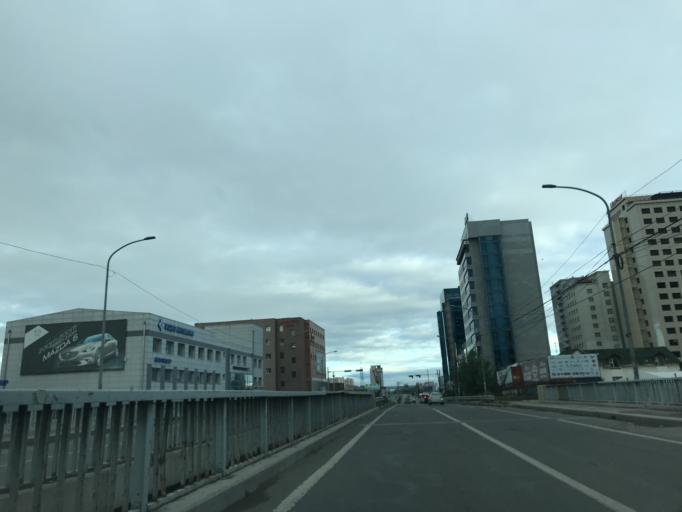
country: MN
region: Ulaanbaatar
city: Ulaanbaatar
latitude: 47.9082
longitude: 106.9326
